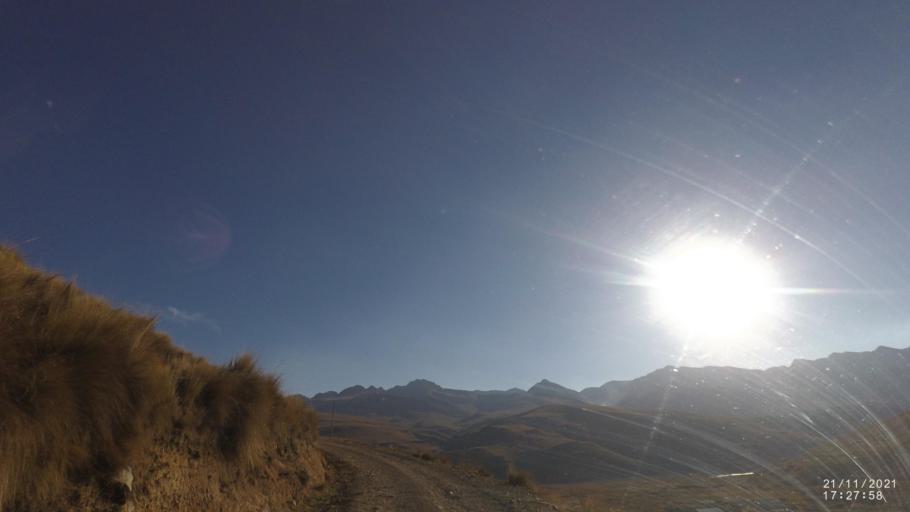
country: BO
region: Cochabamba
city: Cochabamba
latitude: -17.1748
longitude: -66.2593
